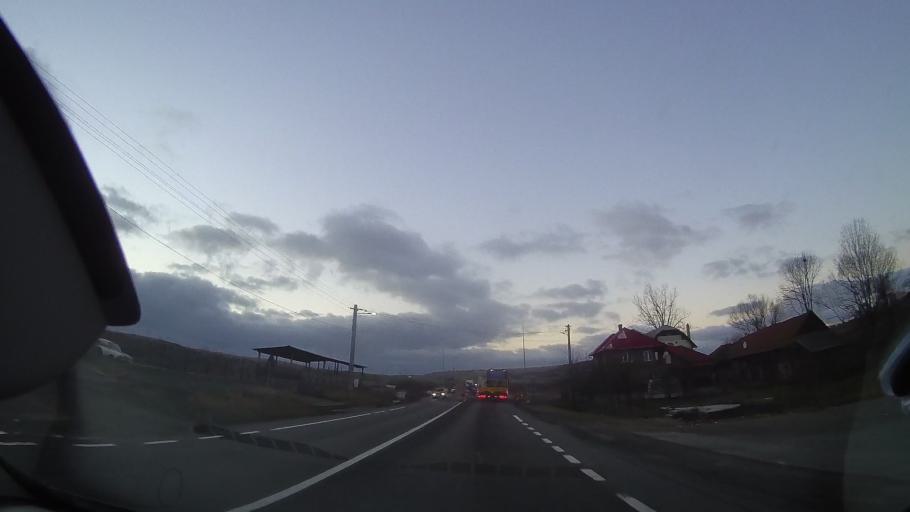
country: RO
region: Cluj
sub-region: Comuna Izvoru Crisului
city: Izvoru Crisului
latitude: 46.8166
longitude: 23.1770
